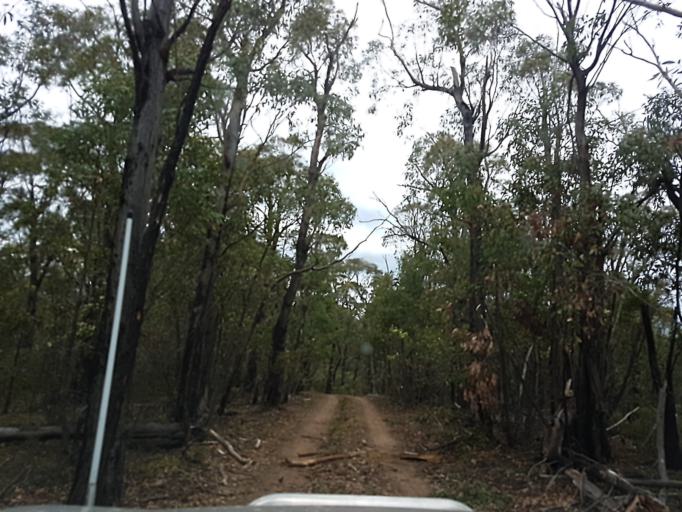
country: AU
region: New South Wales
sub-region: Snowy River
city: Jindabyne
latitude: -36.8635
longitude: 148.2658
